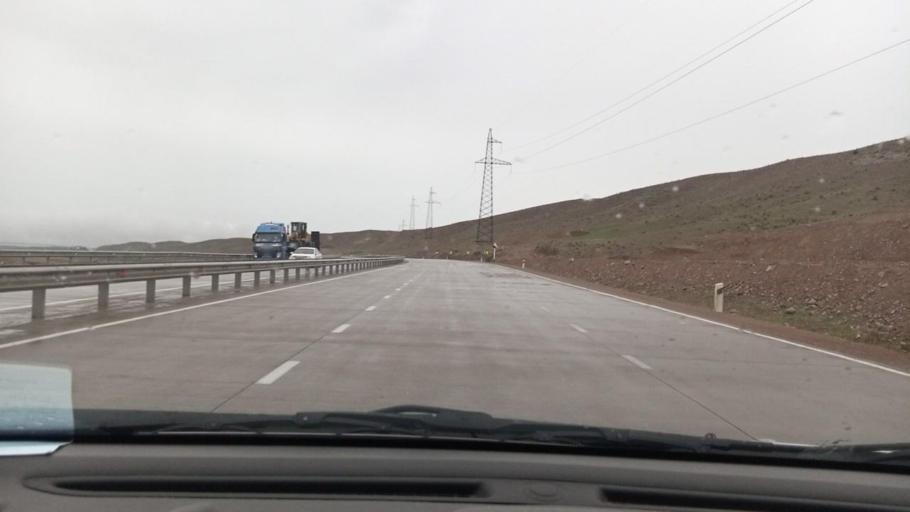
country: UZ
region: Namangan
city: Pop Shahri
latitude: 40.9361
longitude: 70.6952
